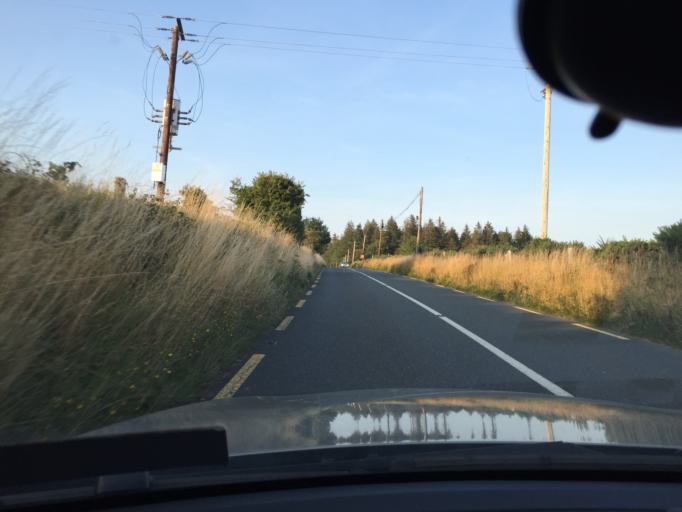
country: IE
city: Newtownmountkennedy
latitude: 53.0733
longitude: -6.2188
